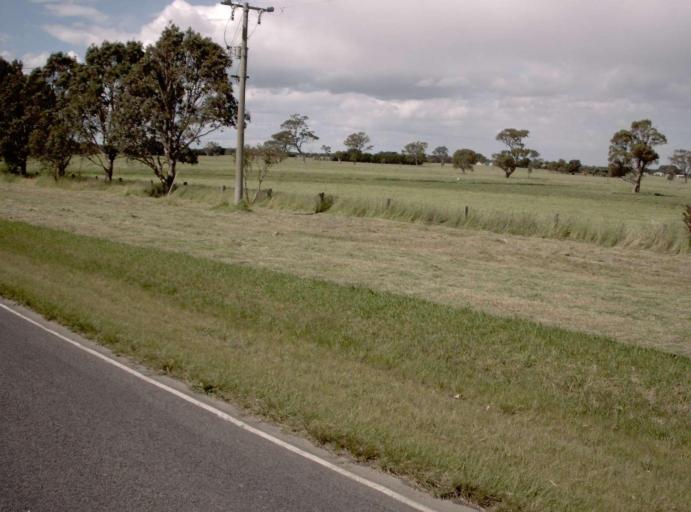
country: AU
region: Victoria
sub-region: Latrobe
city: Traralgon
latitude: -38.1484
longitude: 146.5233
